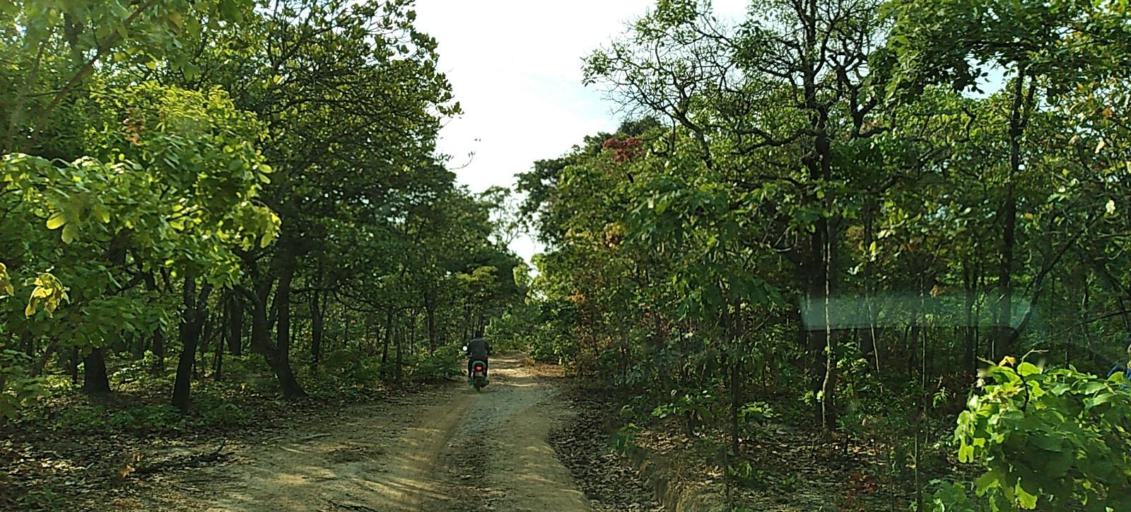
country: ZM
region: Copperbelt
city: Kalulushi
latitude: -12.9562
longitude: 27.6953
